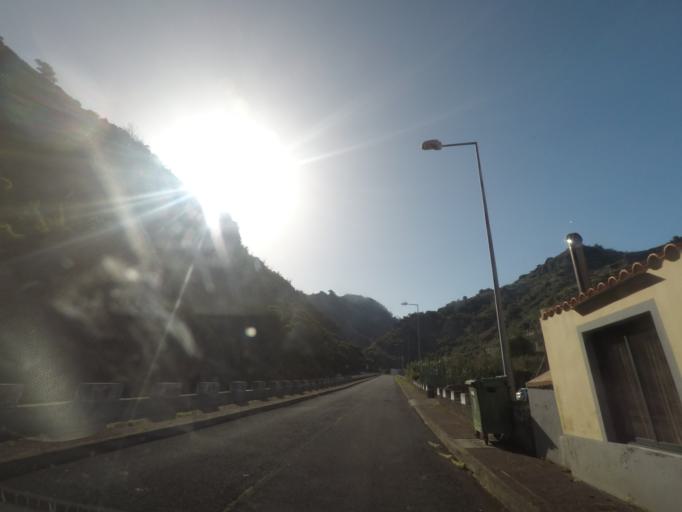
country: PT
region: Madeira
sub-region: Santa Cruz
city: Santa Cruz
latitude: 32.6907
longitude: -16.7983
